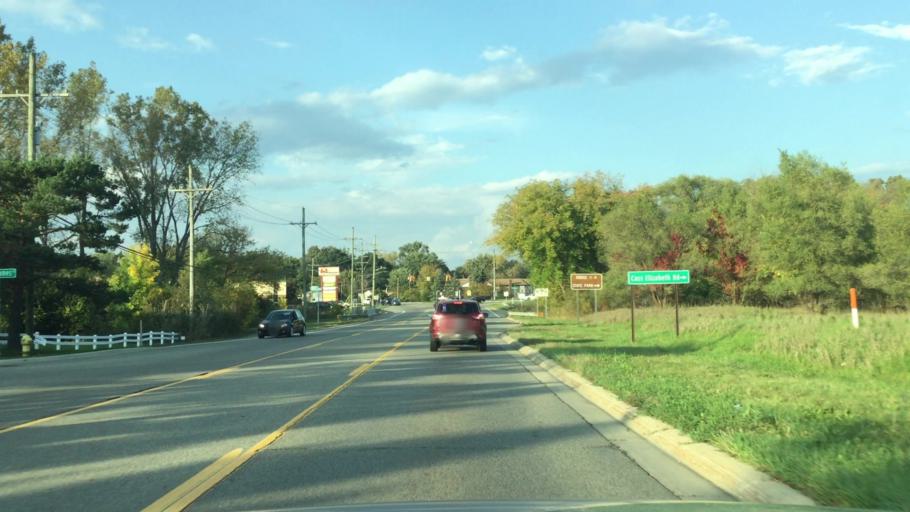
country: US
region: Michigan
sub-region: Oakland County
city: Keego Harbor
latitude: 42.6265
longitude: -83.3956
